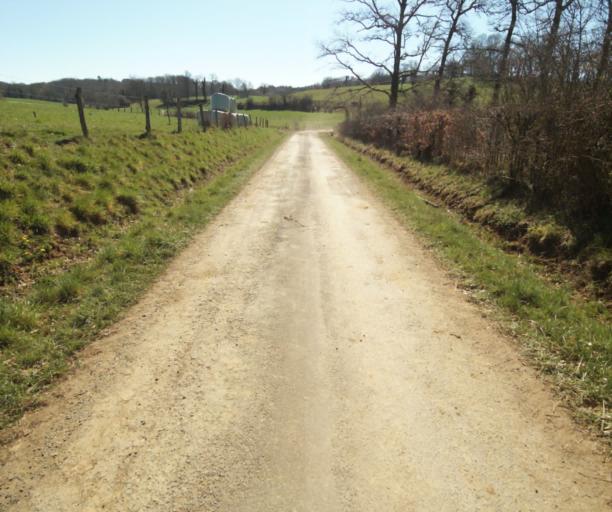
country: FR
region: Limousin
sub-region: Departement de la Correze
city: Chamboulive
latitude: 45.4088
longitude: 1.7431
